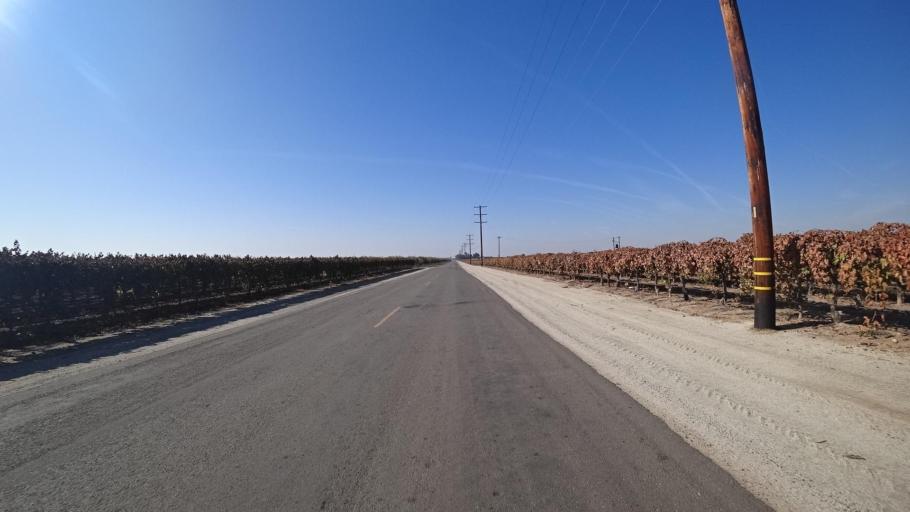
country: US
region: California
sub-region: Kern County
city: McFarland
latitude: 35.7034
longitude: -119.2127
